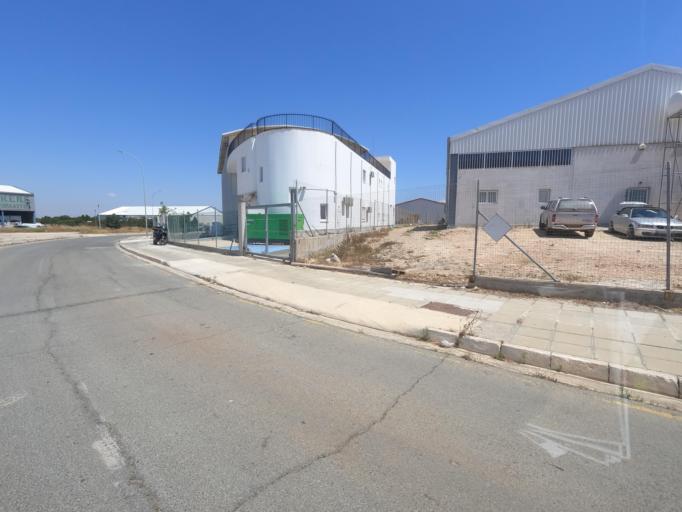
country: CY
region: Ammochostos
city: Frenaros
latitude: 35.0334
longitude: 33.9095
